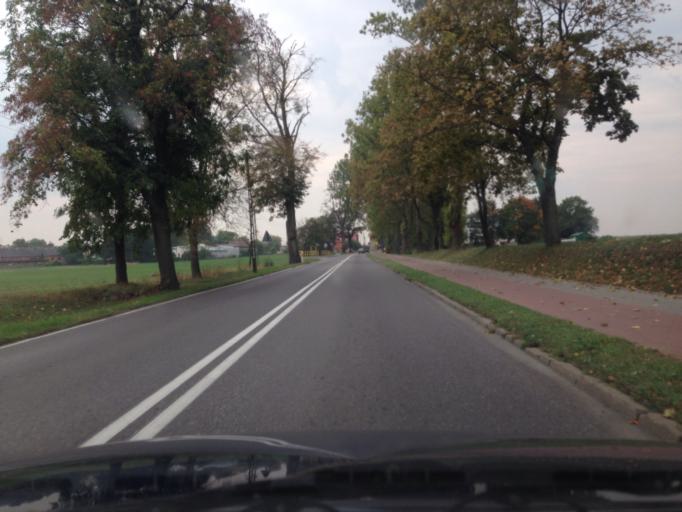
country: PL
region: Pomeranian Voivodeship
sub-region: Powiat kwidzynski
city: Ryjewo
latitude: 53.7833
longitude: 18.9609
